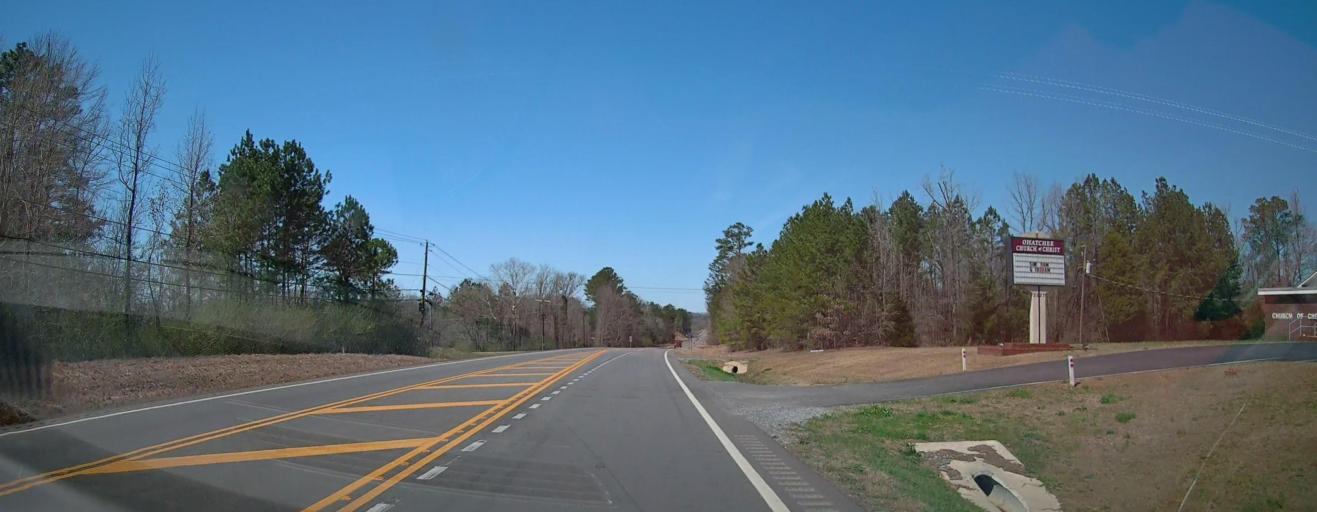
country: US
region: Alabama
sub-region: Calhoun County
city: Ohatchee
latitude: 33.7721
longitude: -85.9839
